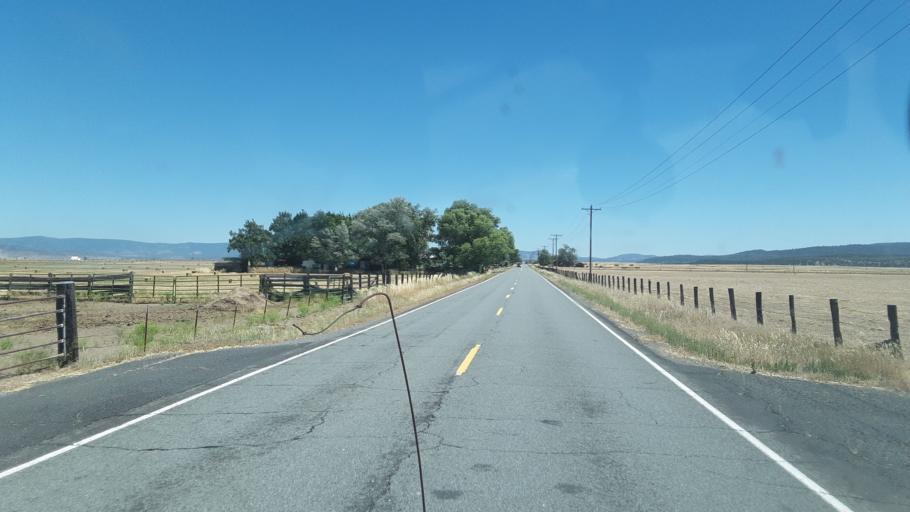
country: US
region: California
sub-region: Shasta County
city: Burney
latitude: 41.1320
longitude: -121.1101
